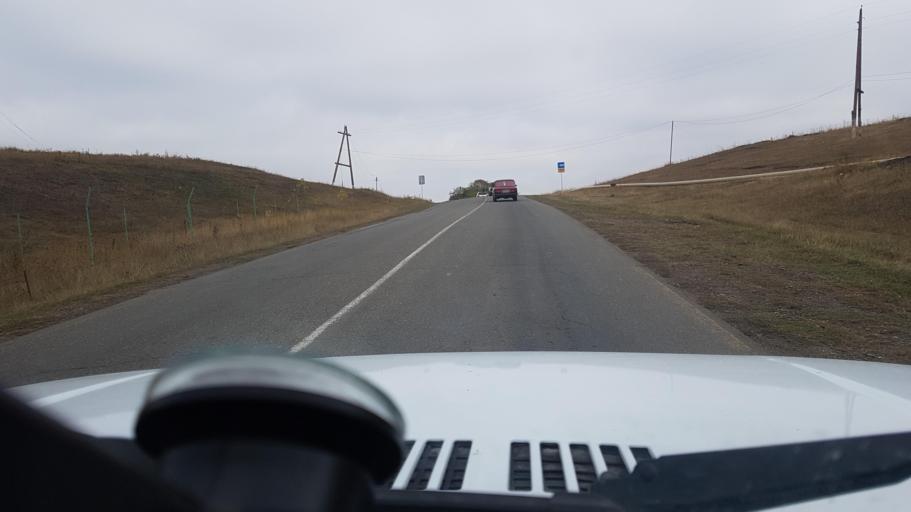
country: AZ
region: Gadabay Rayon
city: Ariqdam
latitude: 40.6189
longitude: 45.8120
